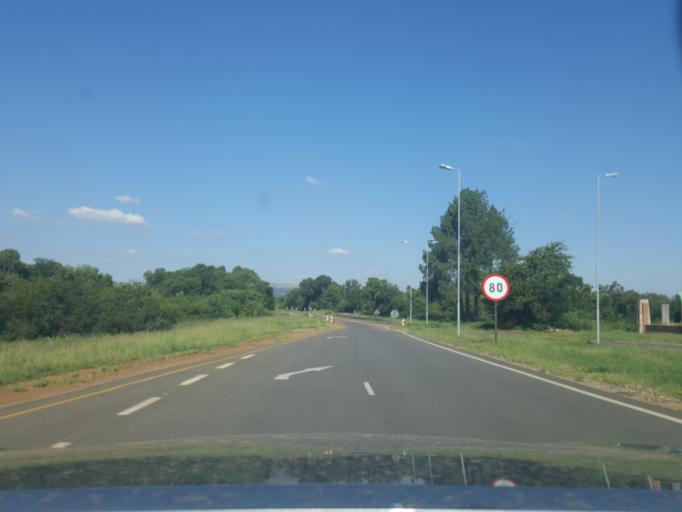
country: ZA
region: Gauteng
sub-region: City of Tshwane Metropolitan Municipality
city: Cullinan
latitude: -25.7544
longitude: 28.3789
